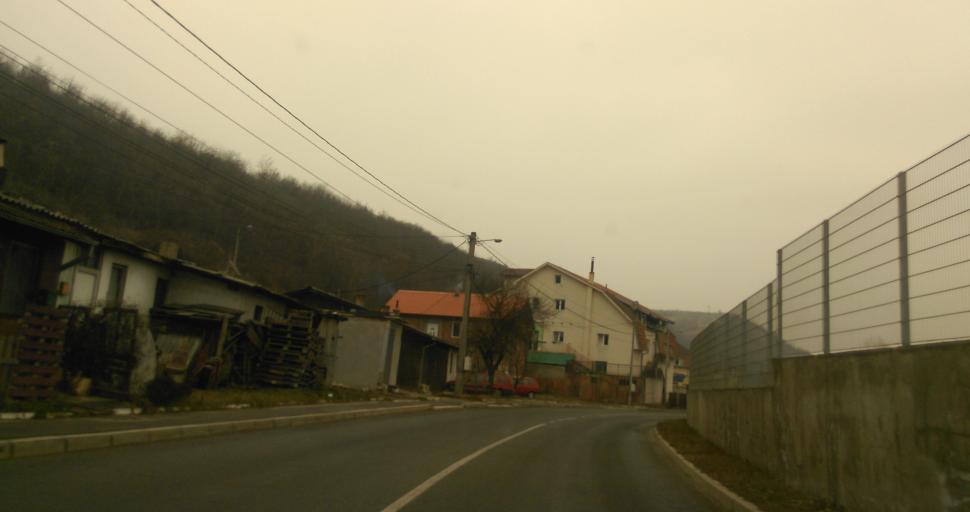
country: RS
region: Central Serbia
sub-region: Belgrade
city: Rakovica
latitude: 44.7251
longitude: 20.4497
